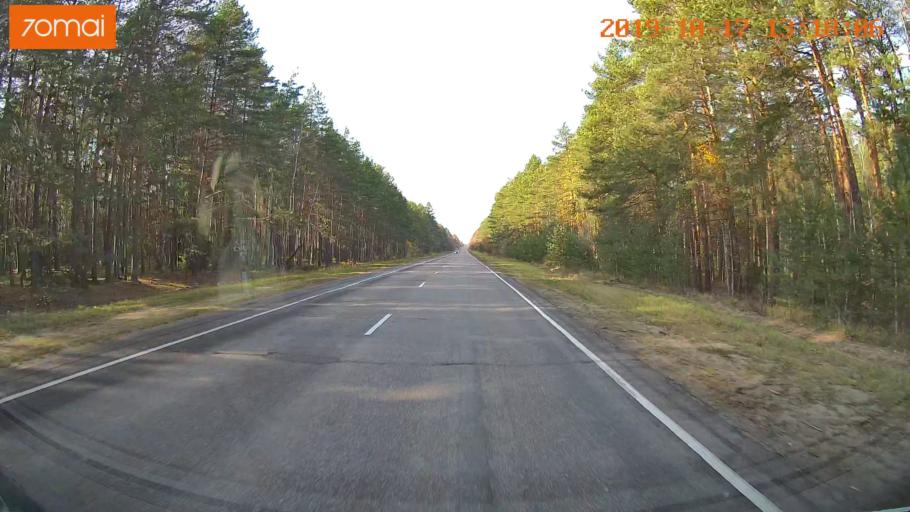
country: RU
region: Rjazan
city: Gus'-Zheleznyy
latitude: 55.0608
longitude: 41.1058
